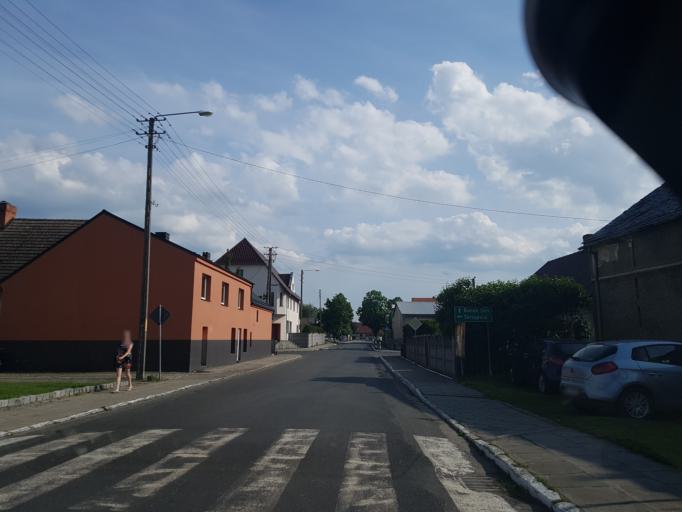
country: PL
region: Lower Silesian Voivodeship
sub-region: Powiat olawski
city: Wierzbno
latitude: 50.8946
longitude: 17.1308
